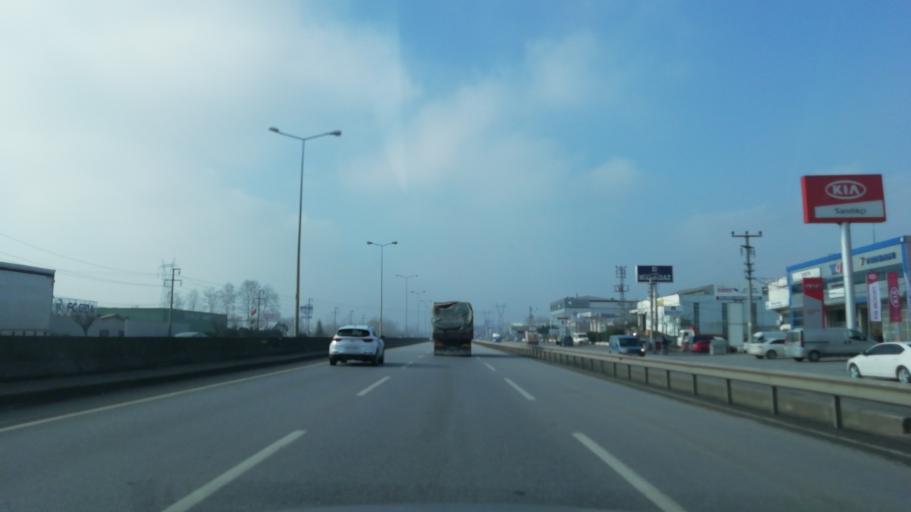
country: TR
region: Sakarya
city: Adapazari
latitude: 40.7377
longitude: 30.4048
